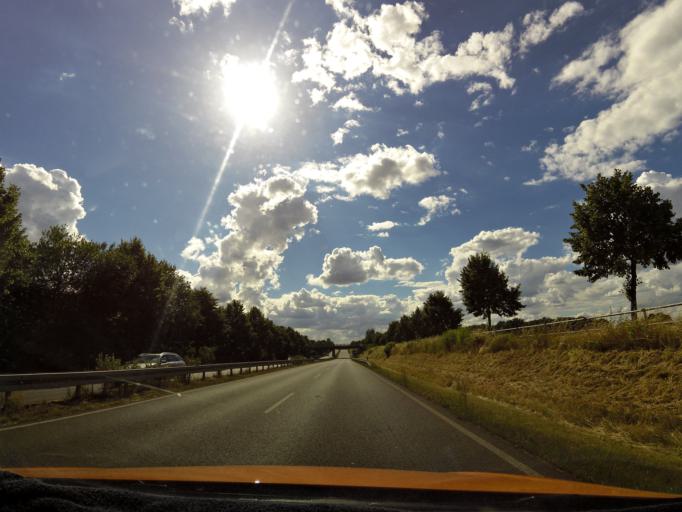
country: DE
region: Berlin
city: Lichtenrade
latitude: 52.3673
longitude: 13.4086
